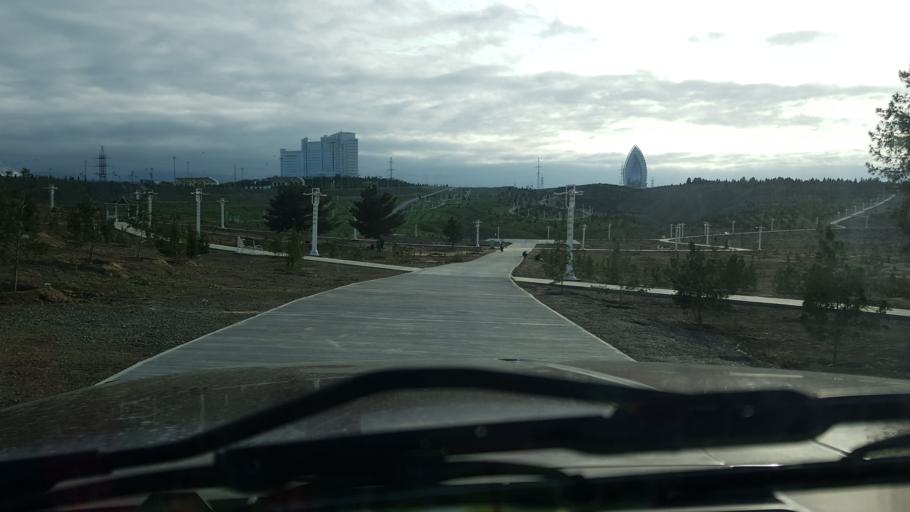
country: TM
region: Ahal
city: Ashgabat
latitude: 37.9356
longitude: 58.3531
